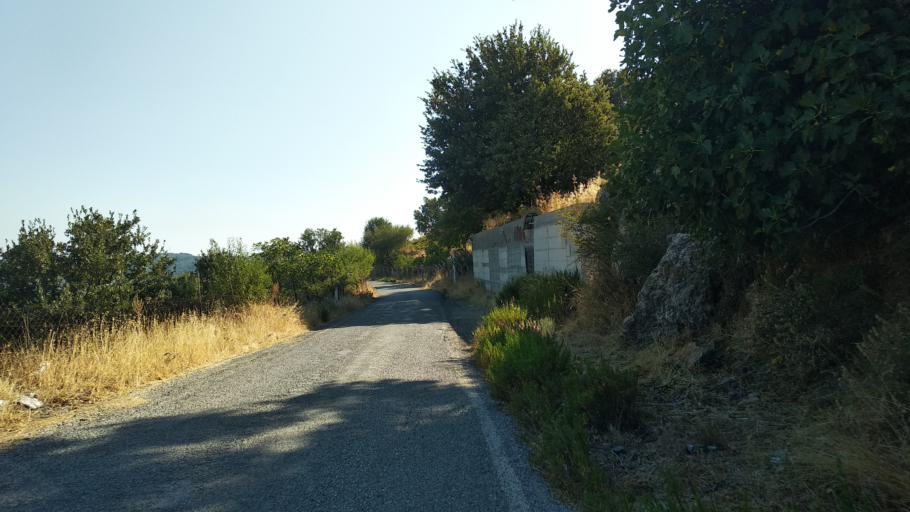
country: TR
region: Izmir
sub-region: Seferihisar
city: Seferhisar
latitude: 38.3187
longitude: 26.9284
